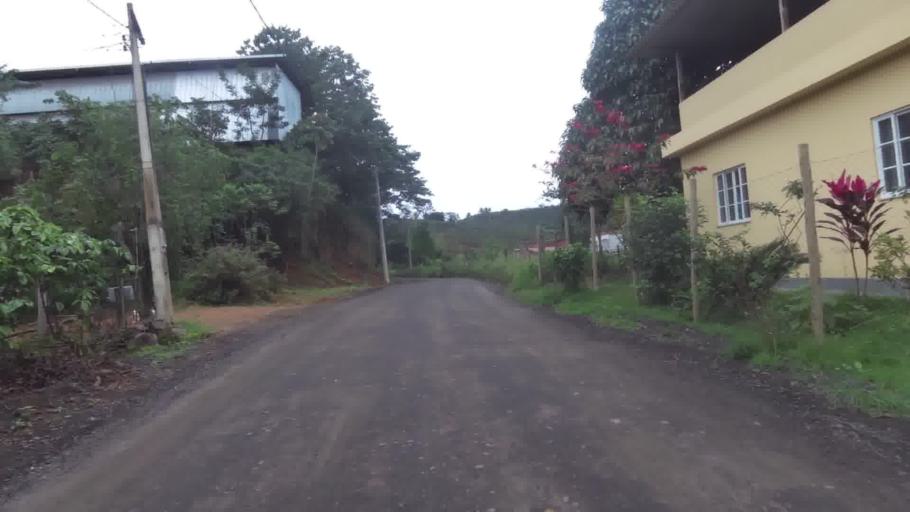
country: BR
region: Espirito Santo
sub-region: Iconha
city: Iconha
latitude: -20.7884
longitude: -40.8217
